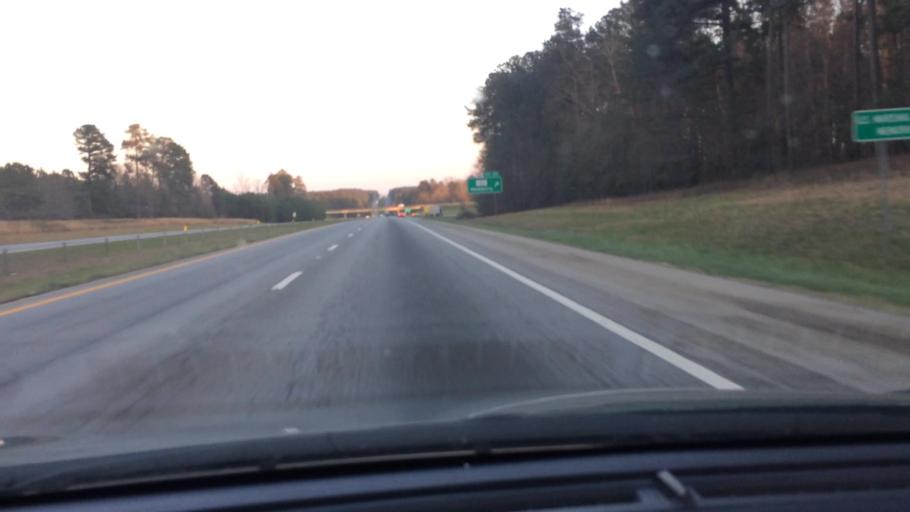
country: US
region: South Carolina
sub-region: Newberry County
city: Newberry
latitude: 34.3340
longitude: -81.6147
